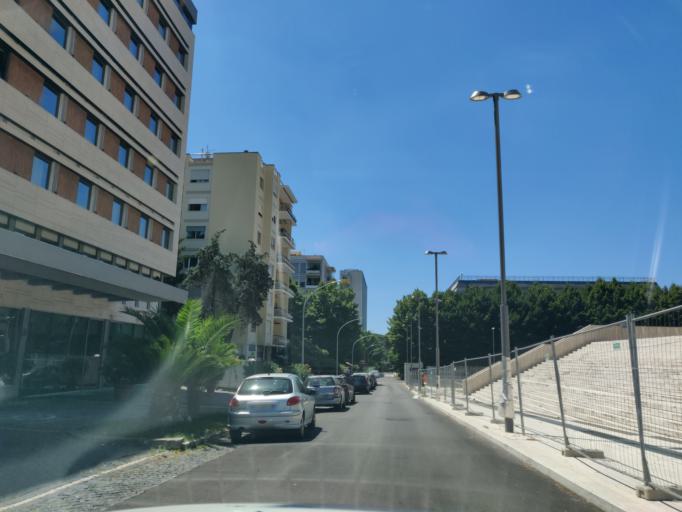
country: IT
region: Latium
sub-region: Citta metropolitana di Roma Capitale
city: Selcetta
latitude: 41.8306
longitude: 12.4730
